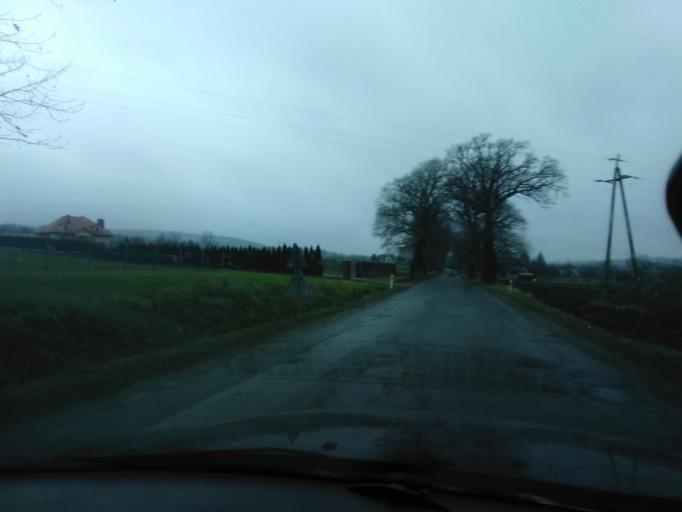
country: PL
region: Subcarpathian Voivodeship
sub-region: Powiat jaroslawski
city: Pruchnik
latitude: 49.9038
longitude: 22.5558
